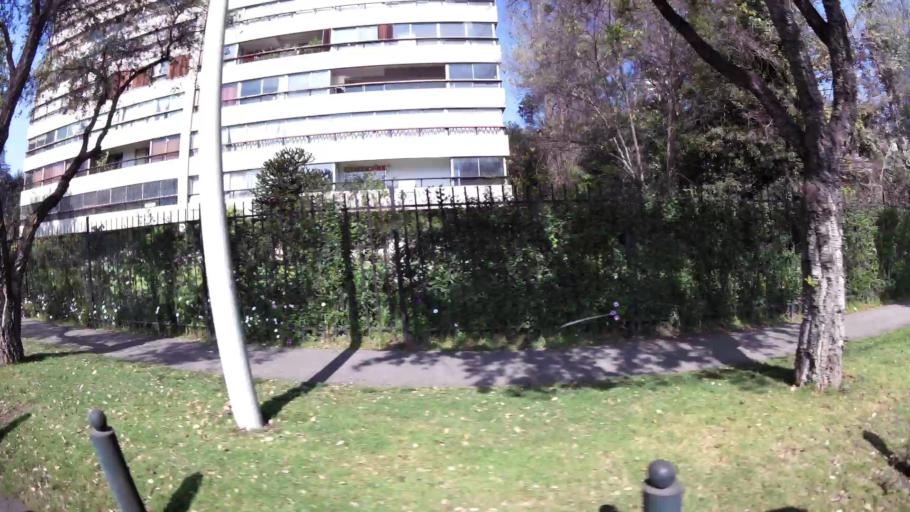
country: CL
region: Santiago Metropolitan
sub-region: Provincia de Santiago
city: Villa Presidente Frei, Nunoa, Santiago, Chile
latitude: -33.4090
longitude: -70.6014
